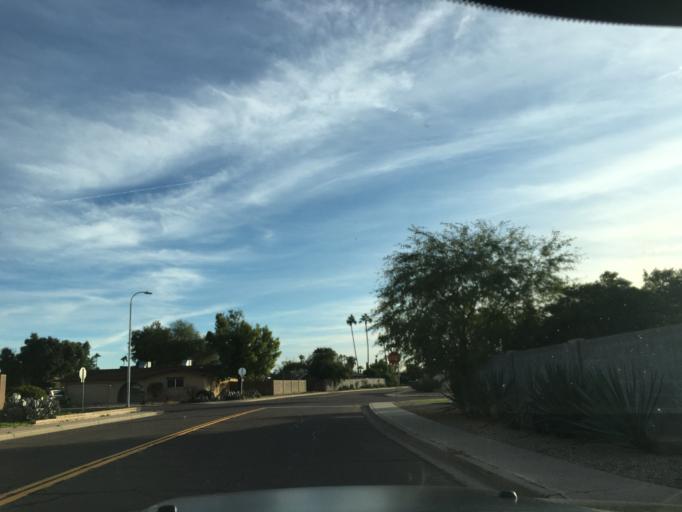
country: US
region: Arizona
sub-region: Maricopa County
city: Tempe
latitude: 33.3696
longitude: -111.9073
